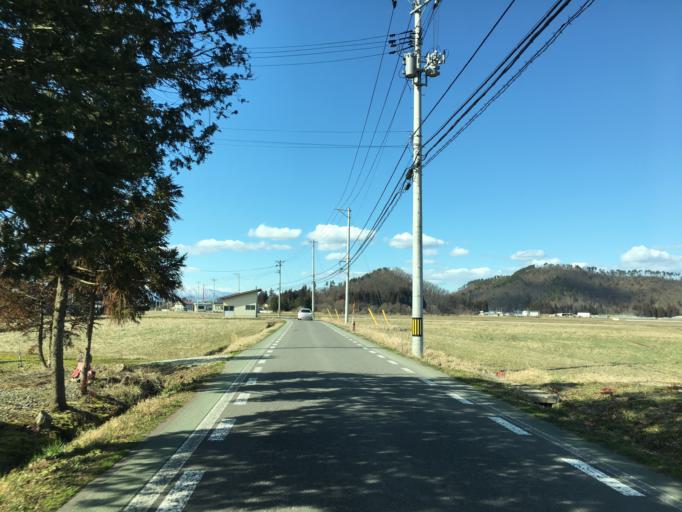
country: JP
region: Yamagata
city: Yonezawa
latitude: 37.9304
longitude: 140.1432
